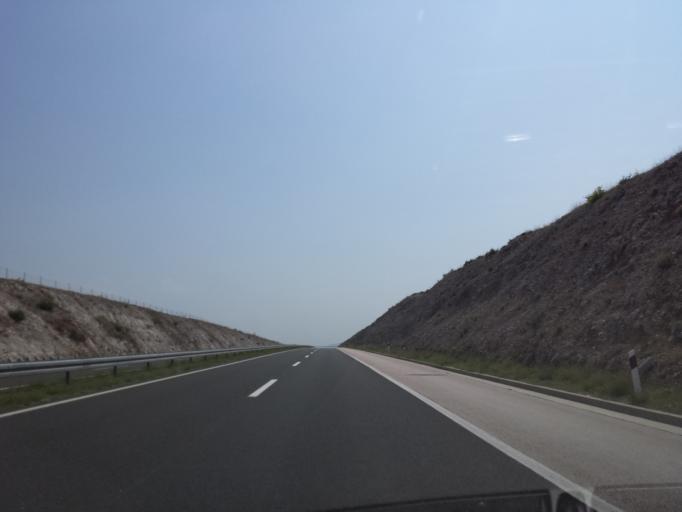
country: HR
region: Zadarska
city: Polaca
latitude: 44.0764
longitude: 15.5130
